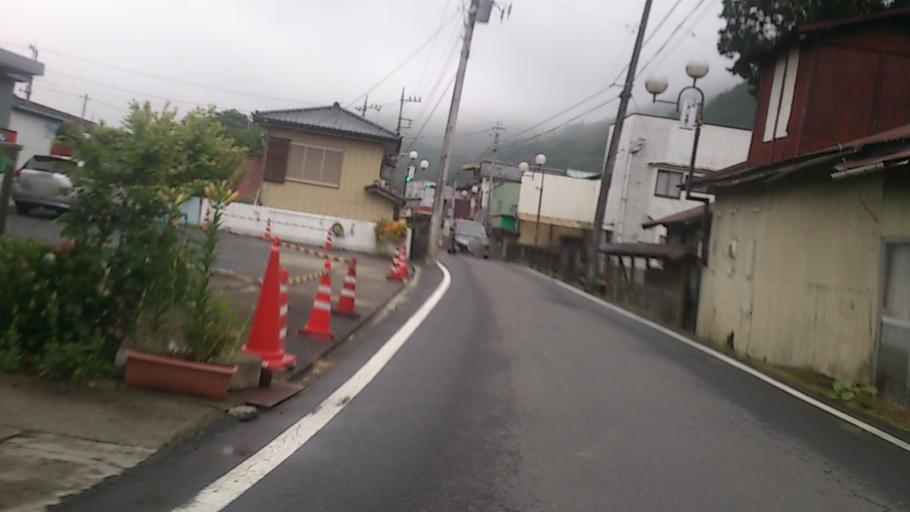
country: JP
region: Ibaraki
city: Daigo
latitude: 36.6626
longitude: 140.3036
